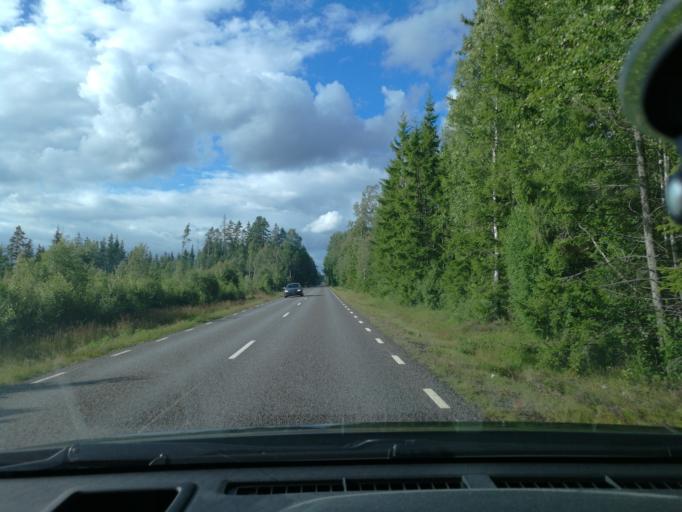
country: SE
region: Kronoberg
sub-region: Vaxjo Kommun
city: Braas
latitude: 57.0707
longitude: 15.0078
